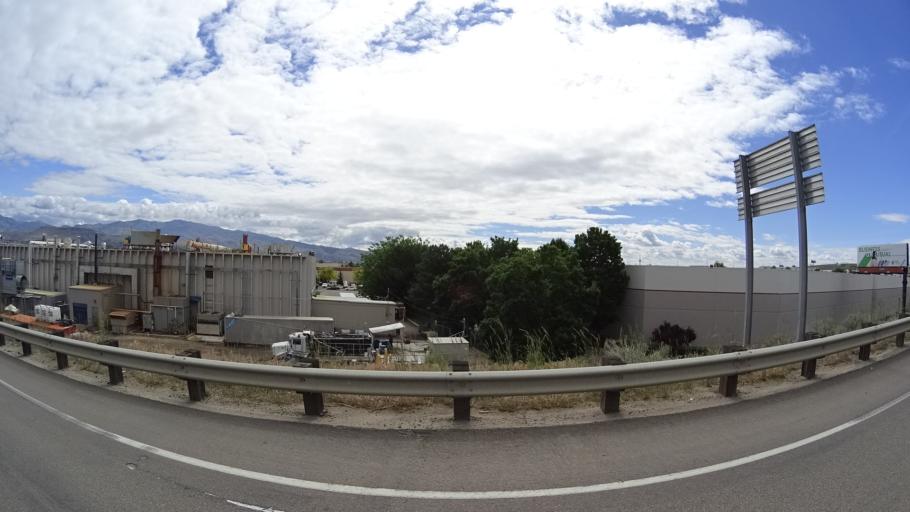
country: US
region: Idaho
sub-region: Ada County
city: Boise
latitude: 43.5707
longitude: -116.1940
